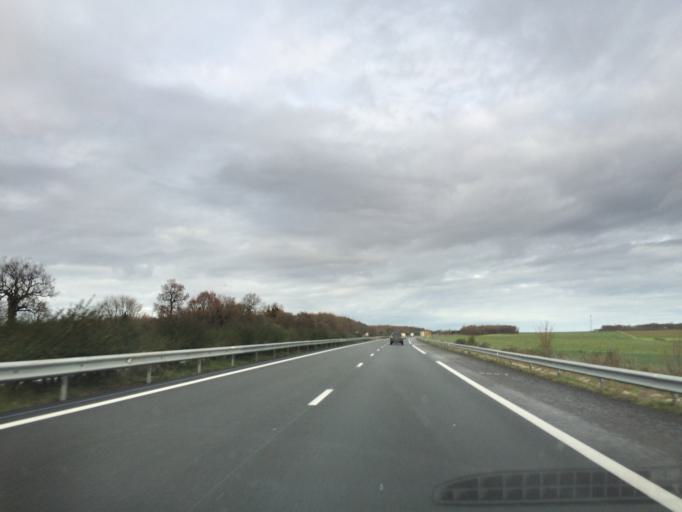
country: FR
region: Poitou-Charentes
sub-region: Departement des Deux-Sevres
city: Beauvoir-sur-Niort
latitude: 46.1720
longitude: -0.5085
